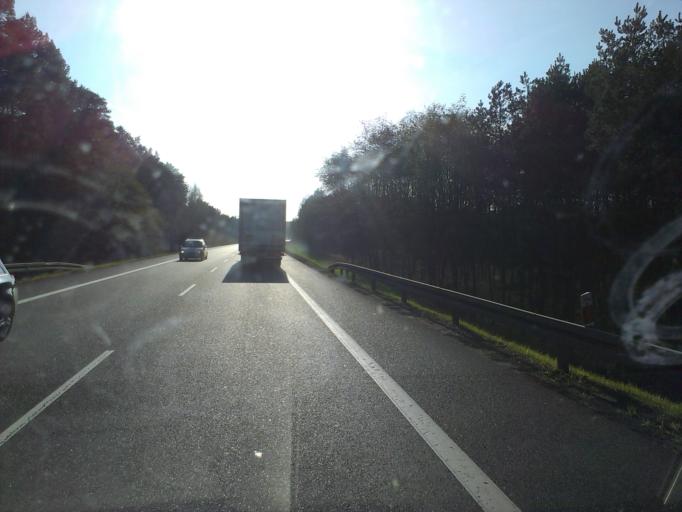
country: PL
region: Lubusz
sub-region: Zielona Gora
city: Zielona Gora
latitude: 51.9714
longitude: 15.5657
